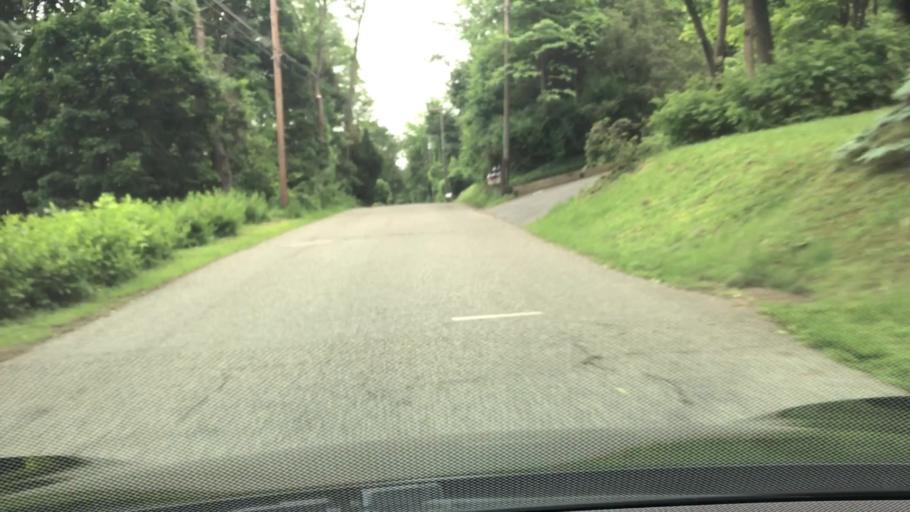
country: US
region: New Jersey
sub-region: Hunterdon County
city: Lebanon
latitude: 40.6331
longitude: -74.8229
